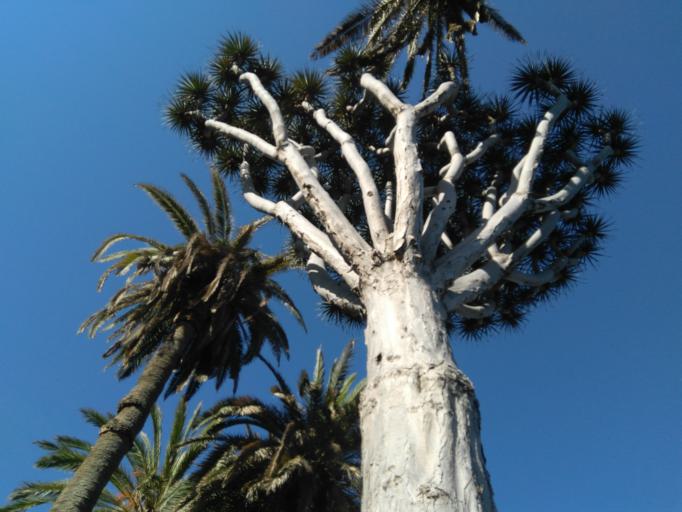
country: ES
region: Canary Islands
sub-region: Provincia de Santa Cruz de Tenerife
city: Realejo Alto
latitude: 28.3969
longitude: -16.5925
